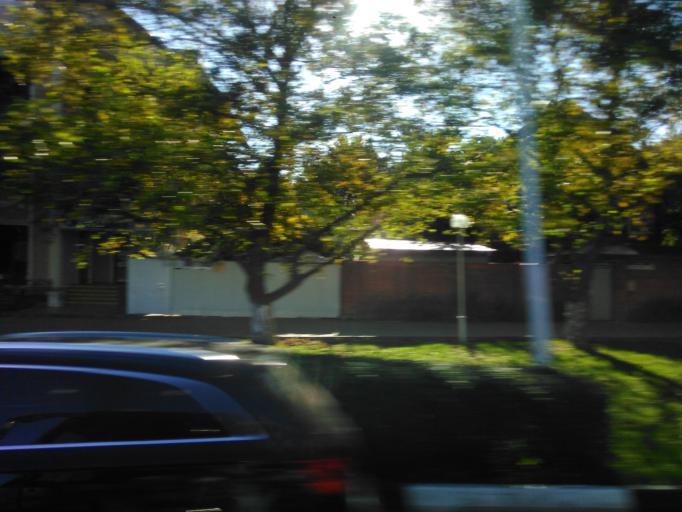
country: RU
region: Krasnodarskiy
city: Gelendzhik
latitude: 44.5555
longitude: 38.0766
